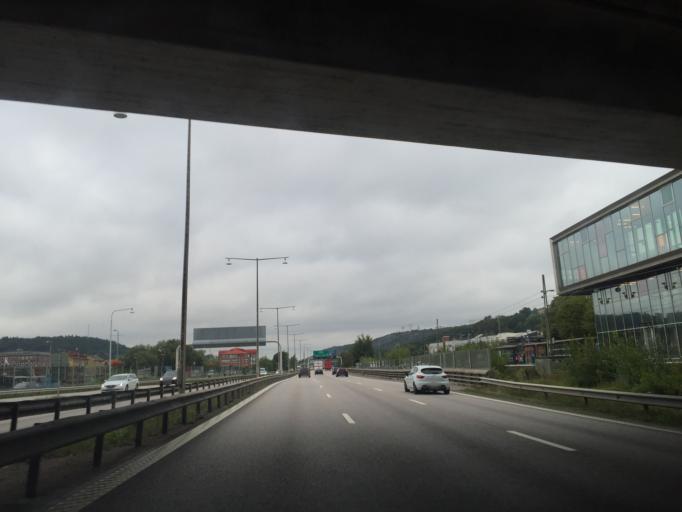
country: SE
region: Vaestra Goetaland
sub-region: Molndal
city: Moelndal
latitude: 57.6555
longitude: 12.0184
